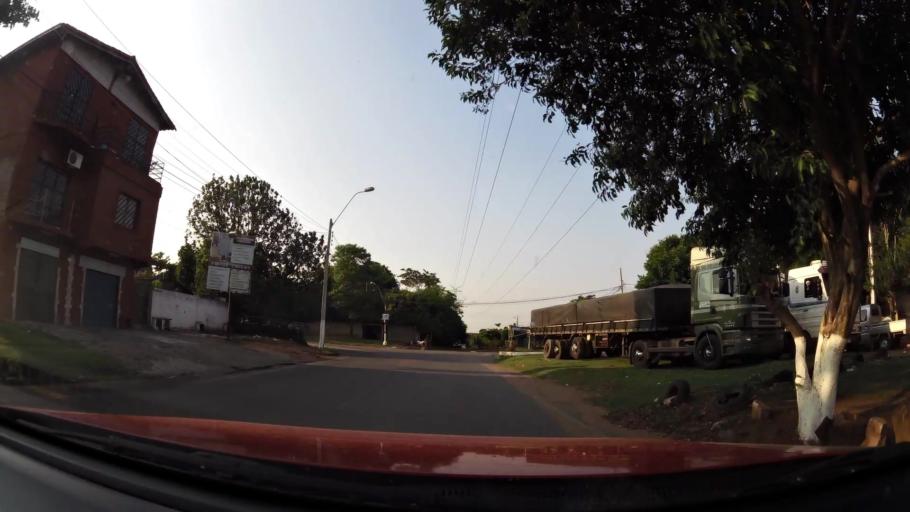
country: PY
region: Central
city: Lambare
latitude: -25.3550
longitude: -57.6088
